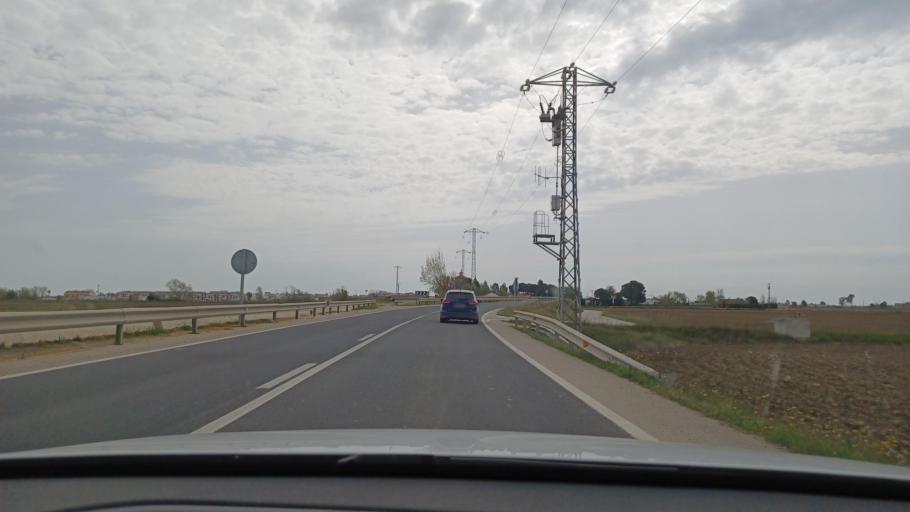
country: ES
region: Catalonia
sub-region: Provincia de Tarragona
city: Deltebre
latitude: 40.7063
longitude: 0.7032
